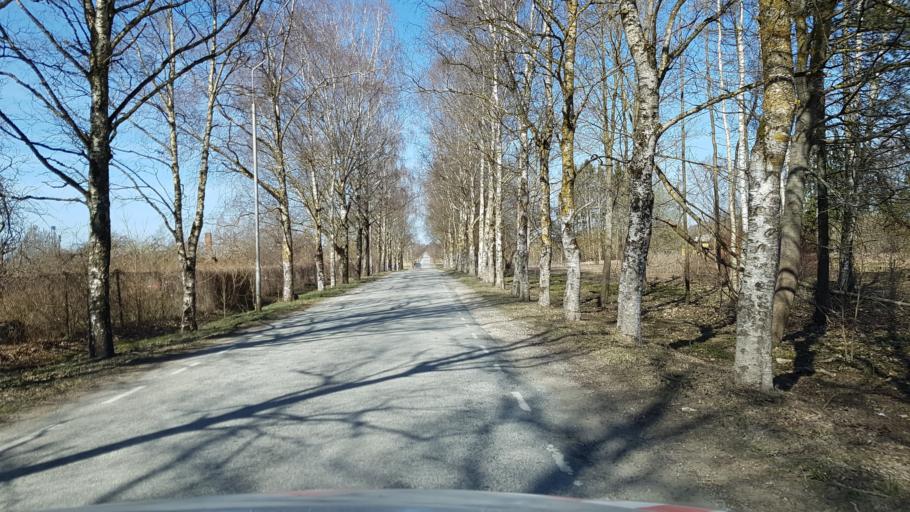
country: EE
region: Laeaene-Virumaa
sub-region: Vinni vald
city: Vinni
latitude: 59.2943
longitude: 26.4276
